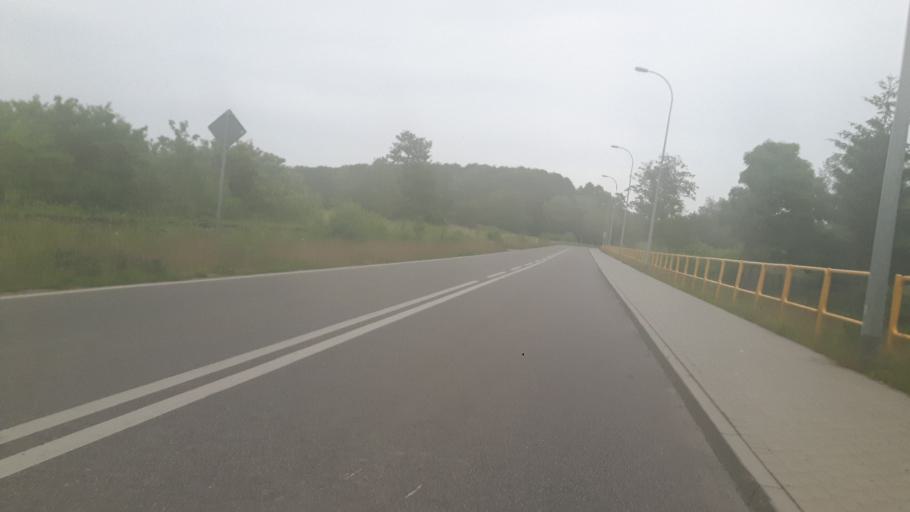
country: PL
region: Warmian-Masurian Voivodeship
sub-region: Powiat elblaski
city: Elblag
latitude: 54.2587
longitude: 19.4021
